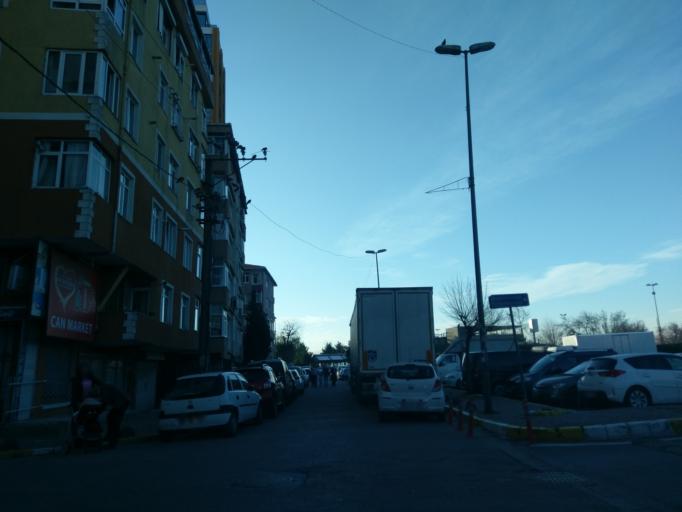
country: TR
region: Istanbul
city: Mahmutbey
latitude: 40.9992
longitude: 28.7654
